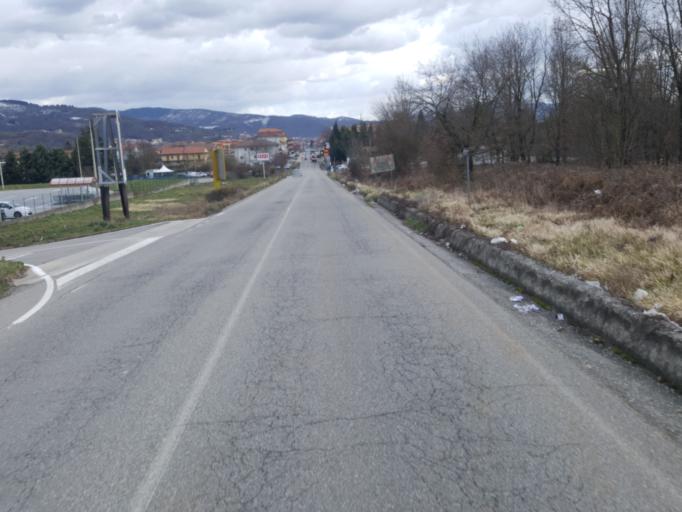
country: IT
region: Calabria
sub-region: Provincia di Cosenza
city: Figline Vegliaturo
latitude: 39.2153
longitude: 16.3077
